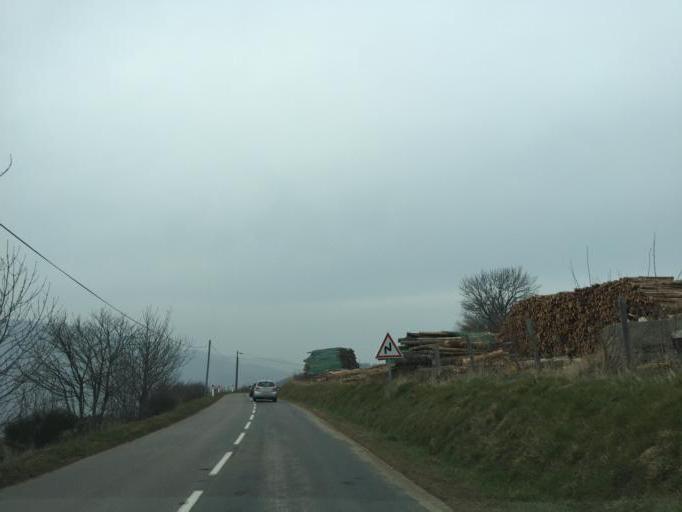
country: FR
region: Rhone-Alpes
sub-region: Departement de la Loire
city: Saint-Chamond
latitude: 45.4074
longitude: 4.5280
